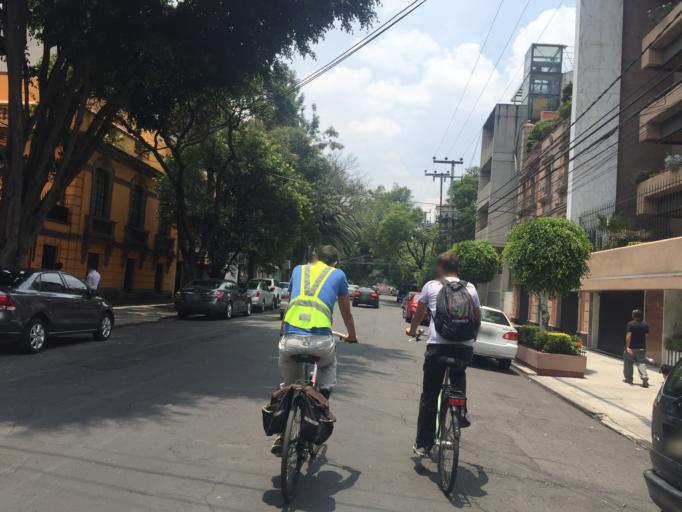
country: MX
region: Mexico City
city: Benito Juarez
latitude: 19.4165
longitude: -99.1614
